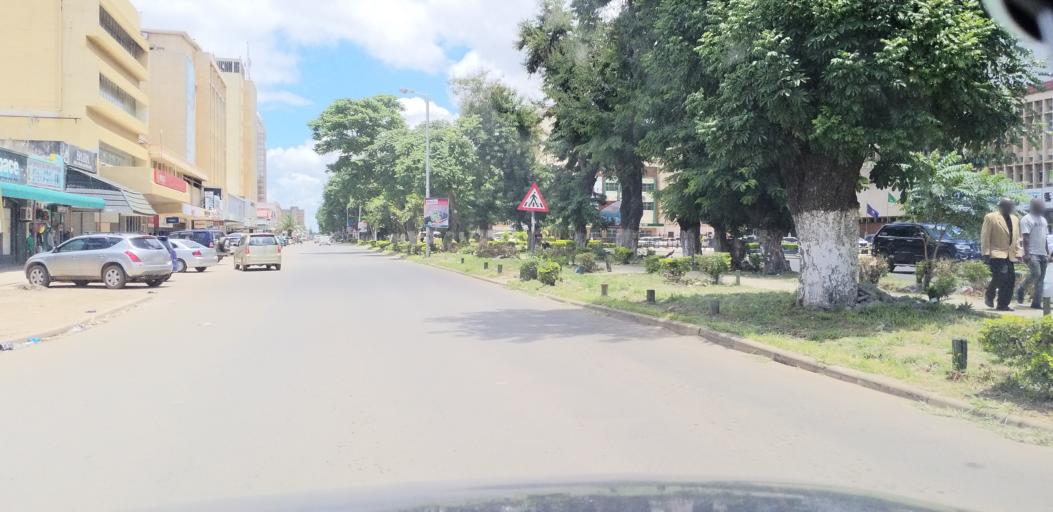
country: ZM
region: Lusaka
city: Lusaka
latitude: -15.4222
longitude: 28.2825
